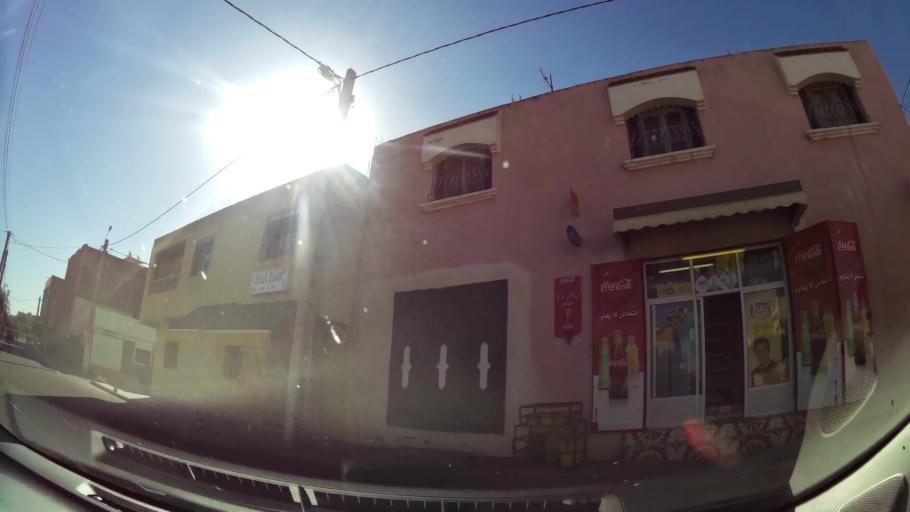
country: MA
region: Oriental
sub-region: Oujda-Angad
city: Oujda
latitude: 34.6536
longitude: -1.8968
